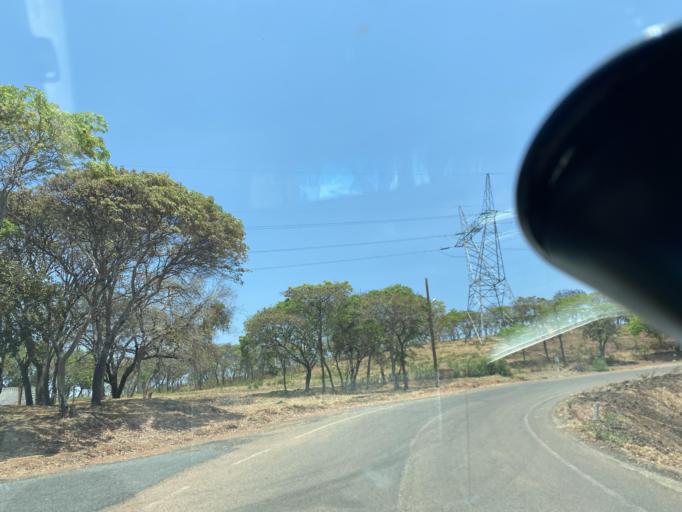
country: ZM
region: Lusaka
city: Kafue
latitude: -15.8665
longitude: 28.4579
